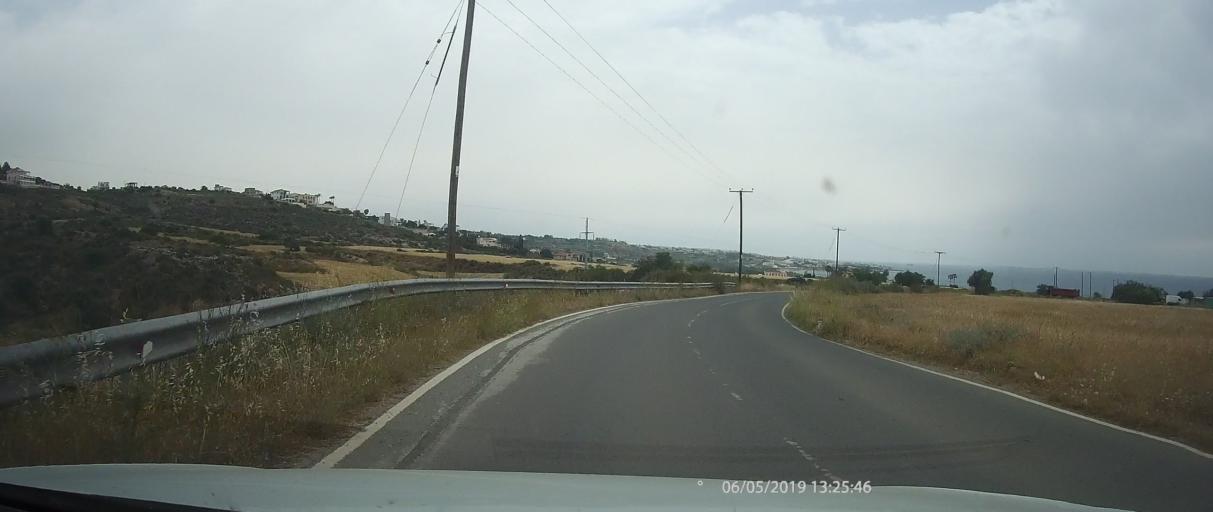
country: CY
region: Pafos
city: Pegeia
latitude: 34.8549
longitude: 32.3863
